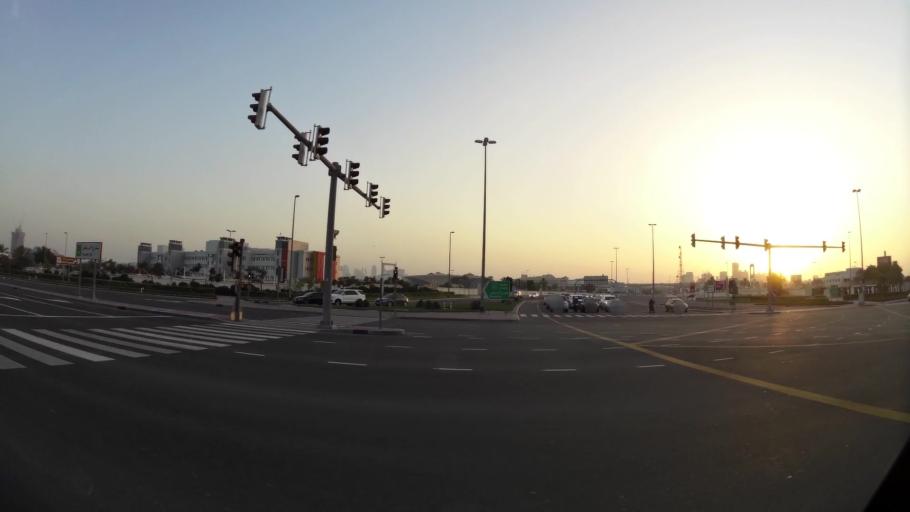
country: AE
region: Ash Shariqah
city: Sharjah
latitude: 25.2458
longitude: 55.3219
